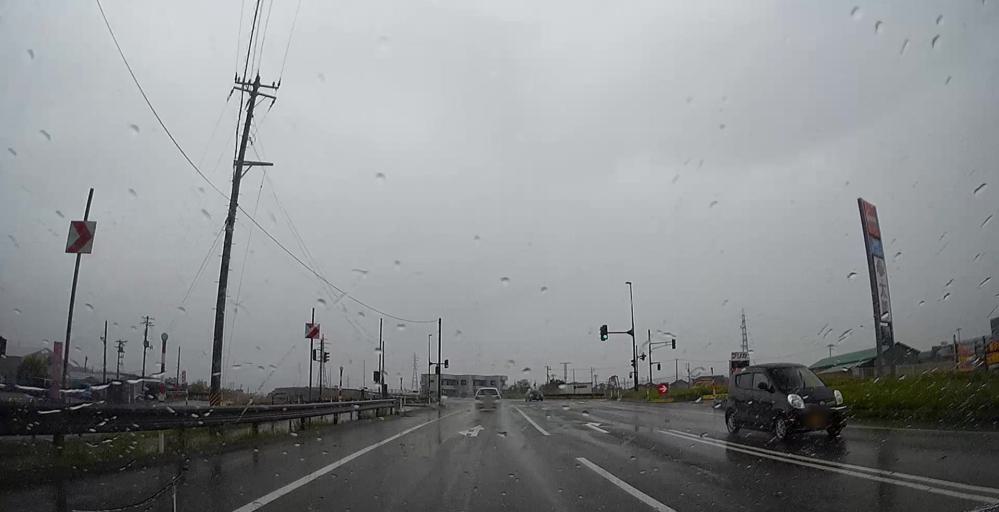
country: JP
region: Niigata
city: Kashiwazaki
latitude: 37.3887
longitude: 138.5901
